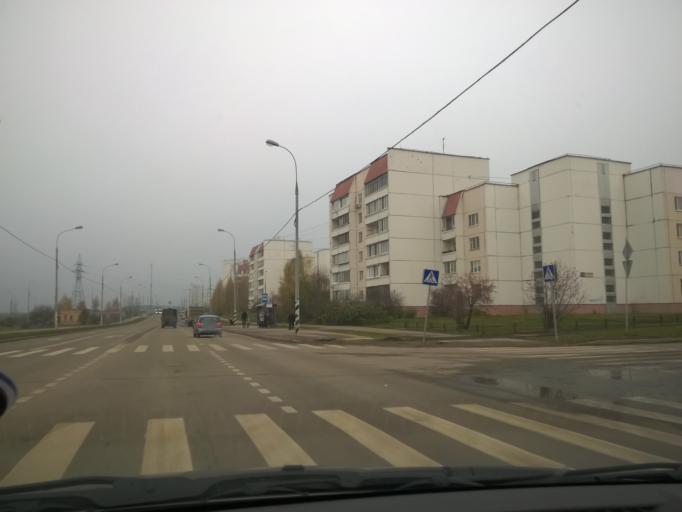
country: RU
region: Moskovskaya
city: Kommunarka
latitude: 55.5269
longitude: 37.5158
